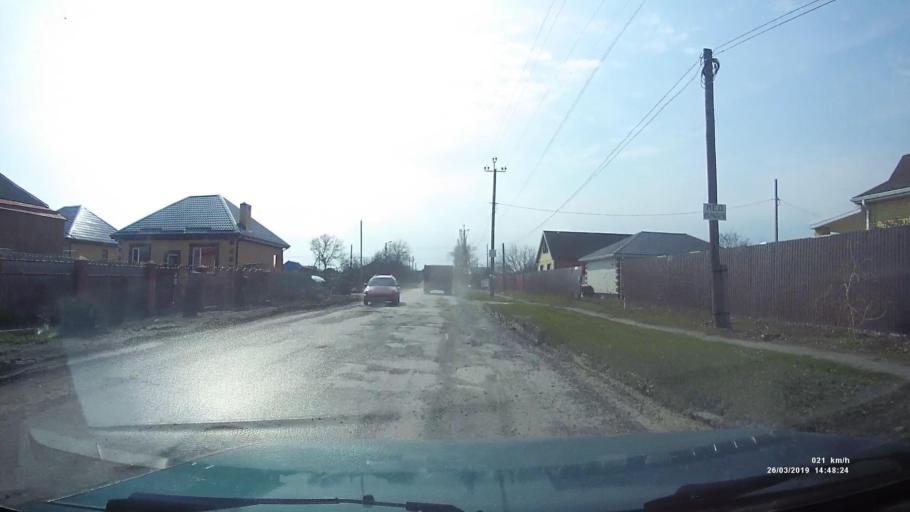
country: RU
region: Rostov
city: Novobessergenovka
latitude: 47.1908
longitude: 38.8550
